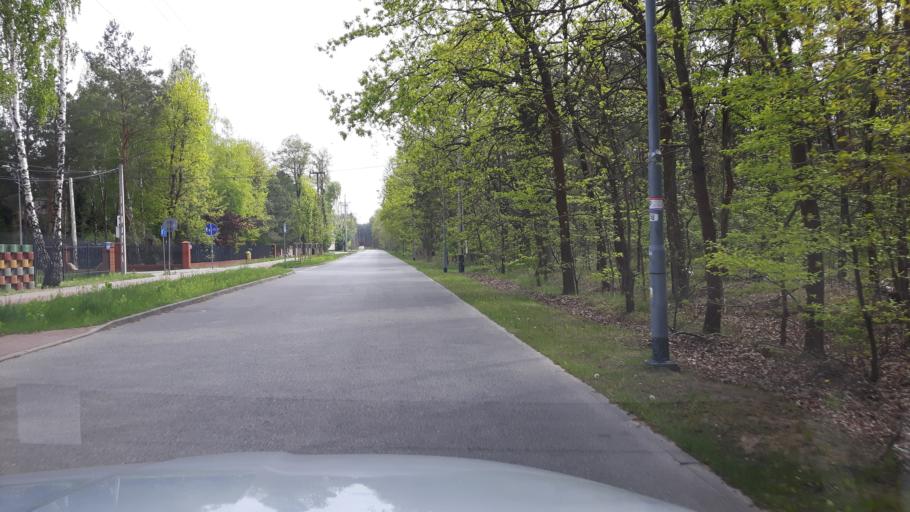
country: PL
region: Masovian Voivodeship
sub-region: Warszawa
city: Wesola
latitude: 52.2491
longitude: 21.1987
